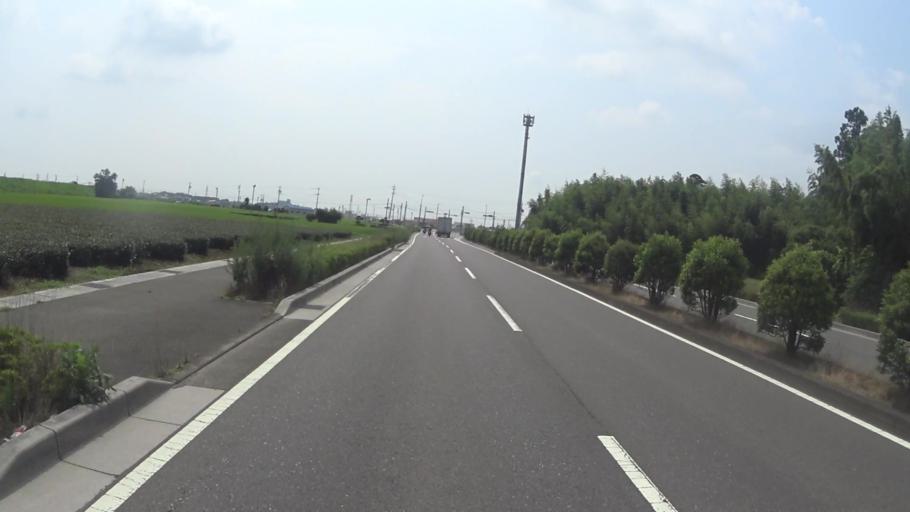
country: JP
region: Mie
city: Kameyama
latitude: 34.8963
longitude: 136.5052
